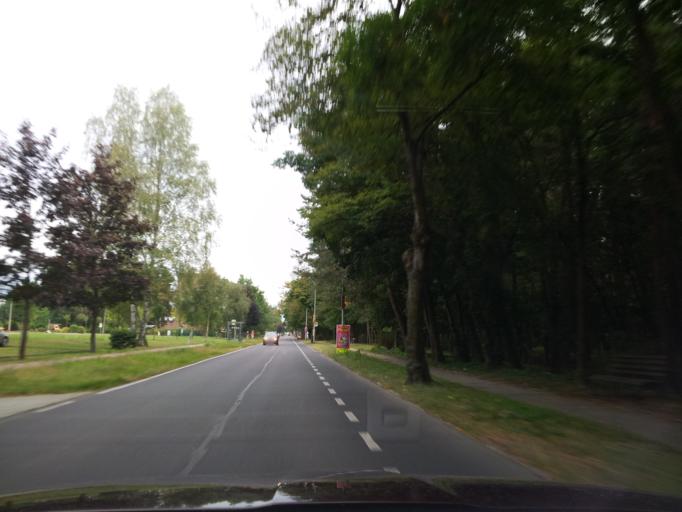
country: DE
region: Brandenburg
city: Luckenwalde
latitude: 52.1061
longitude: 13.1484
